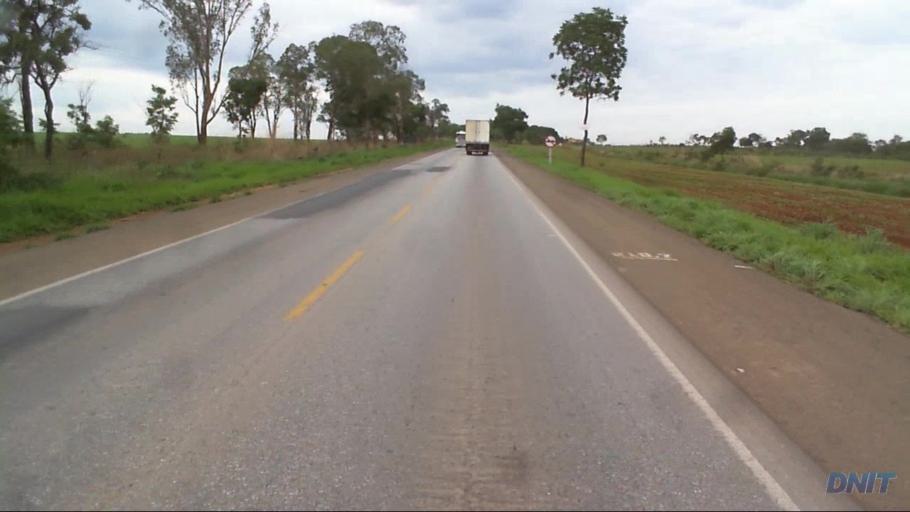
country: BR
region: Goias
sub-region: Uruacu
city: Uruacu
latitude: -14.6183
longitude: -49.1705
